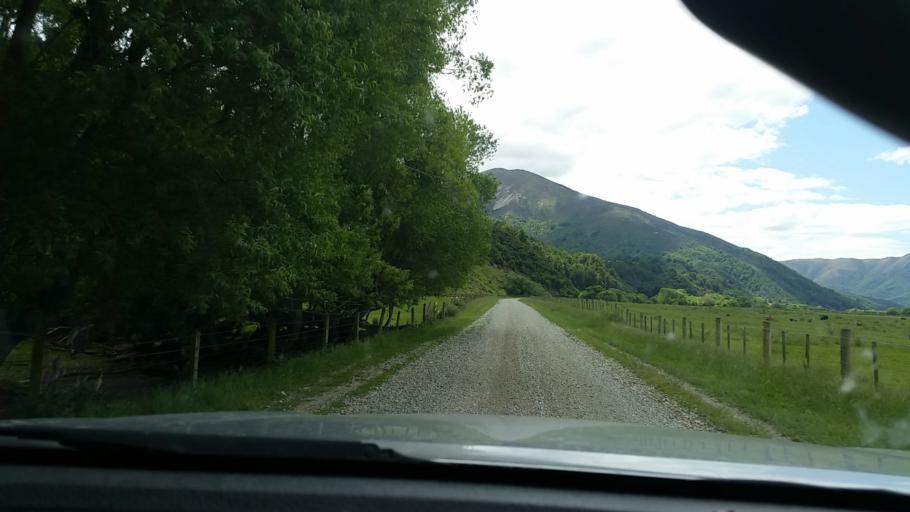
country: NZ
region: Otago
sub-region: Queenstown-Lakes District
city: Kingston
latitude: -45.6784
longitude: 168.6273
